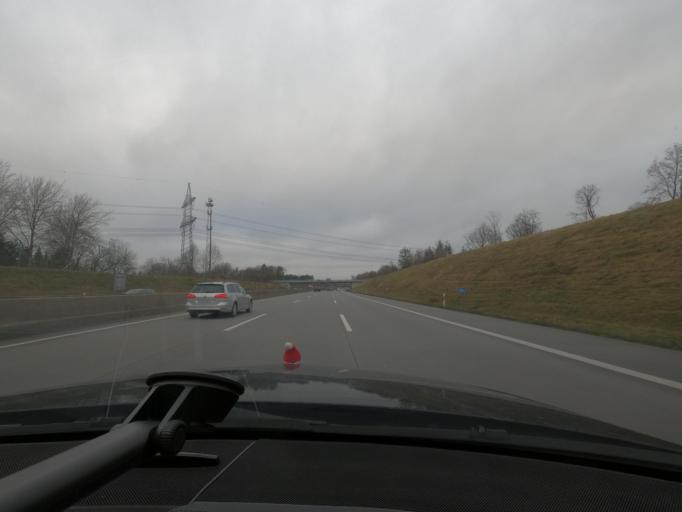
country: DE
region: Schleswig-Holstein
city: Quickborn
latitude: 53.7229
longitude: 9.9393
